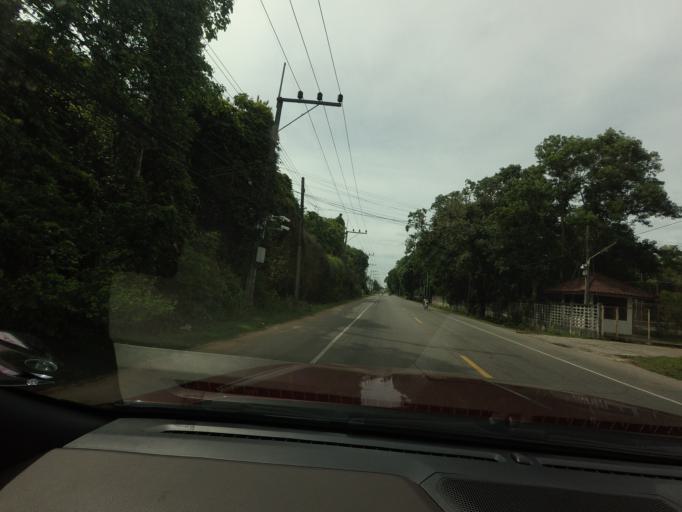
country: TH
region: Narathiwat
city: Tak Bai
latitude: 6.2448
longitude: 102.0739
